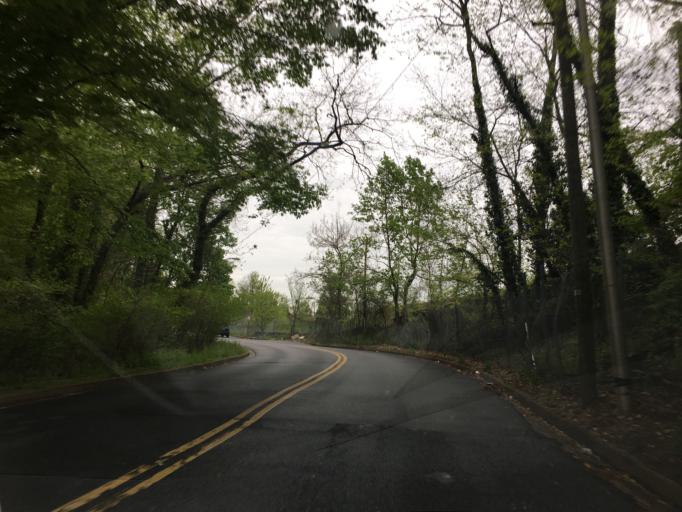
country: US
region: Maryland
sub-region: Baltimore County
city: Charlestown
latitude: 39.2907
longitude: -76.6973
